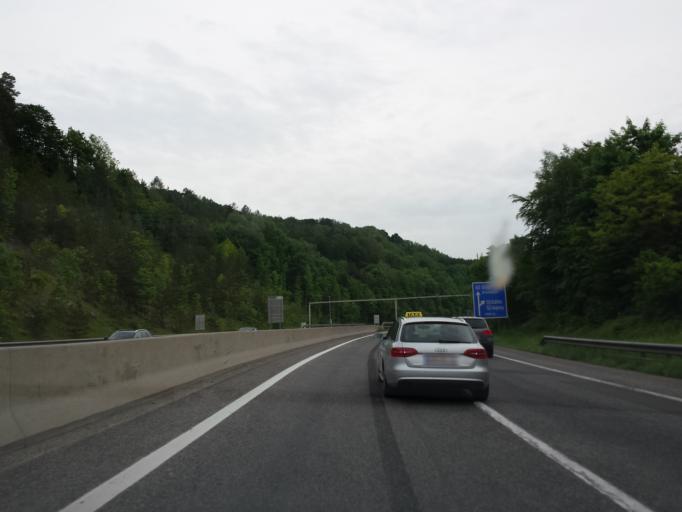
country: AT
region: Lower Austria
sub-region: Politischer Bezirk Neunkirchen
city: Grimmenstein
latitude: 47.6246
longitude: 16.1326
